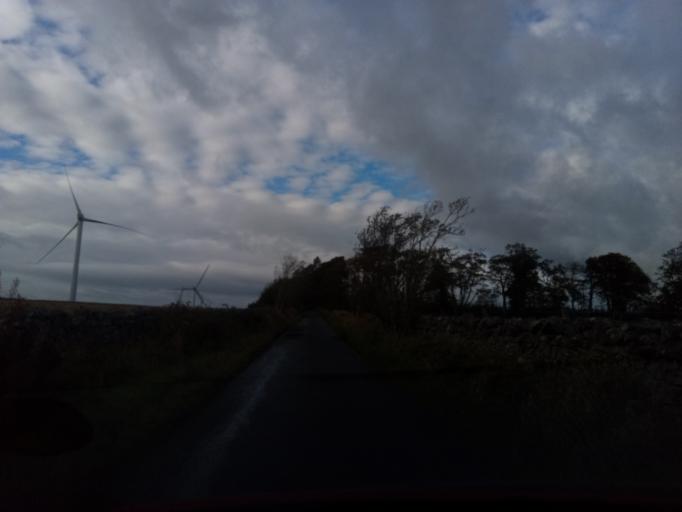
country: GB
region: Scotland
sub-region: The Scottish Borders
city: Galashiels
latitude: 55.6855
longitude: -2.8466
